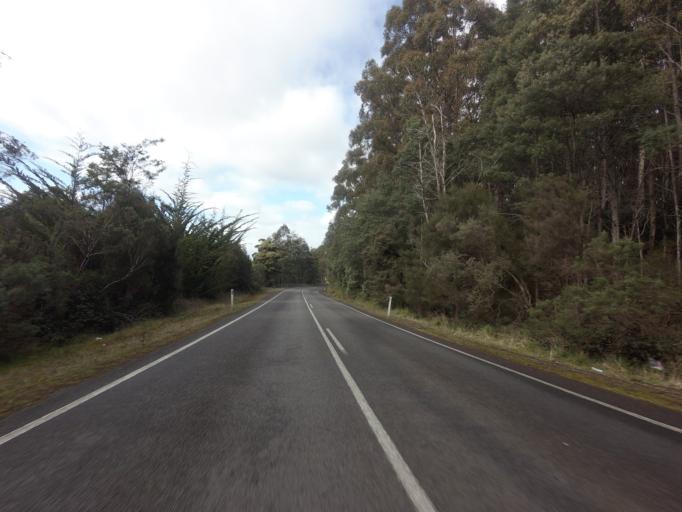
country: AU
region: Tasmania
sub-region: Huon Valley
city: Geeveston
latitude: -43.4081
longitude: 146.9589
